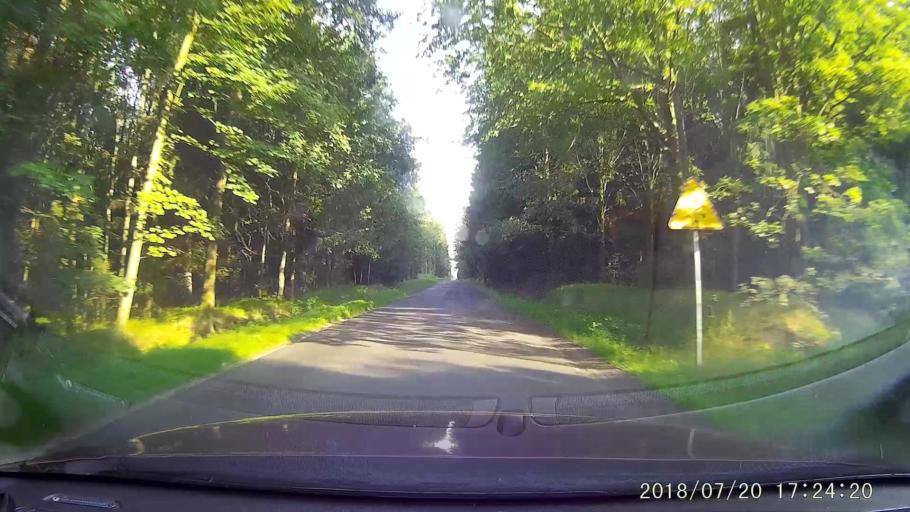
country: PL
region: Lower Silesian Voivodeship
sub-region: Powiat lubanski
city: Lesna
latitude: 50.9706
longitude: 15.2946
